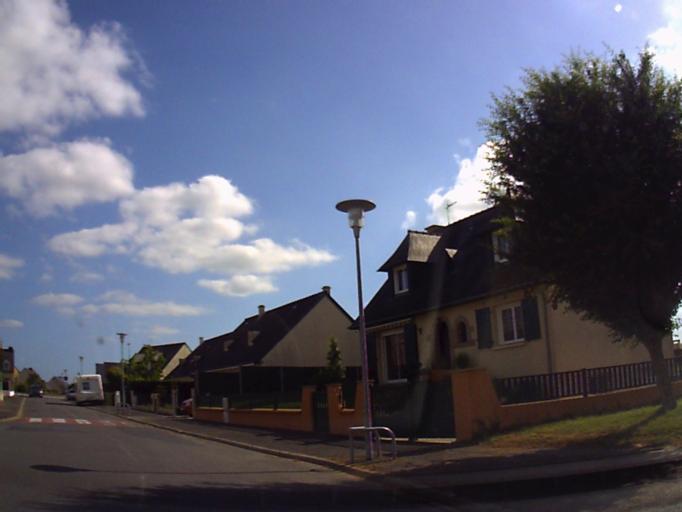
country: FR
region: Brittany
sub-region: Departement d'Ille-et-Vilaine
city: Bedee
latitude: 48.1798
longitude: -1.9510
